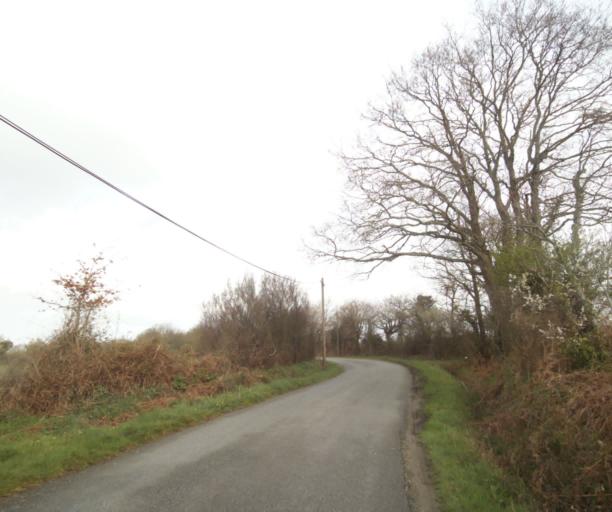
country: FR
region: Pays de la Loire
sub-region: Departement de la Loire-Atlantique
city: Bouvron
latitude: 47.4029
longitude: -1.8624
